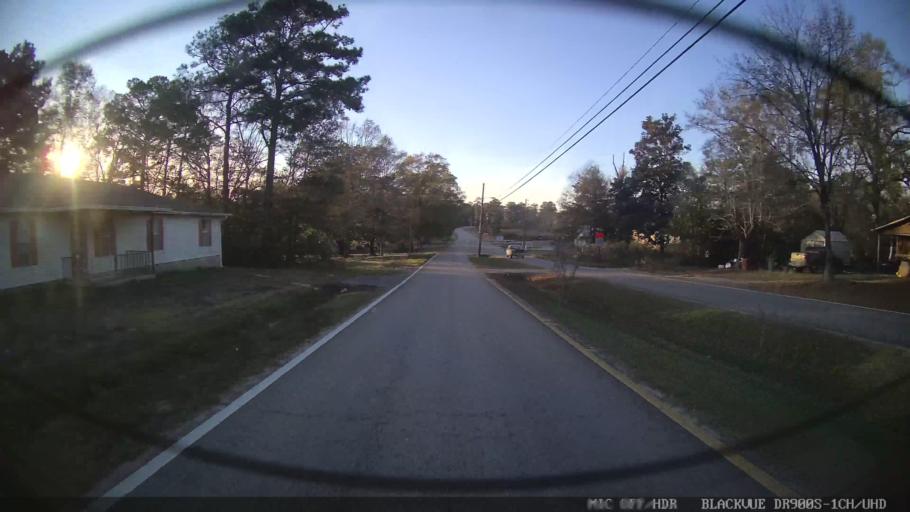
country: US
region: Mississippi
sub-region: Lamar County
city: Lumberton
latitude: 31.0058
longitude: -89.4644
